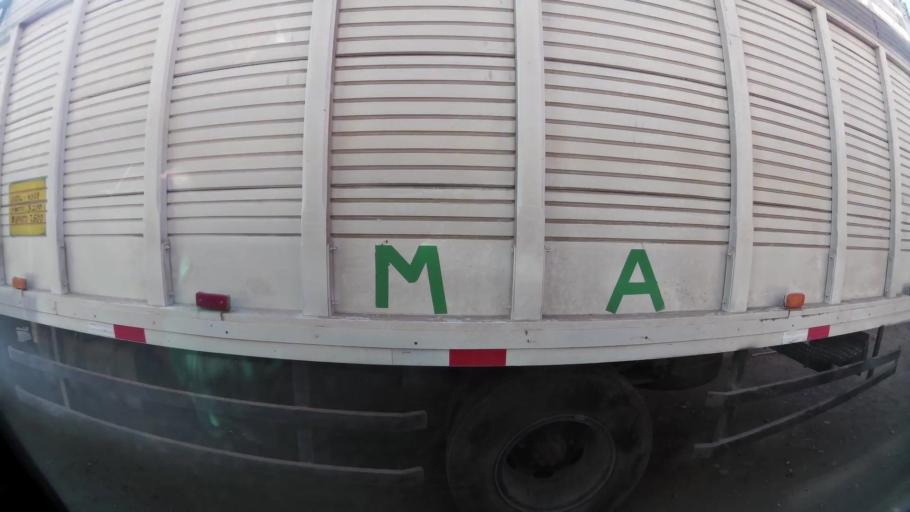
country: PE
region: Lima
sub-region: Huaura
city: Huacho
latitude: -11.1240
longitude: -77.6123
